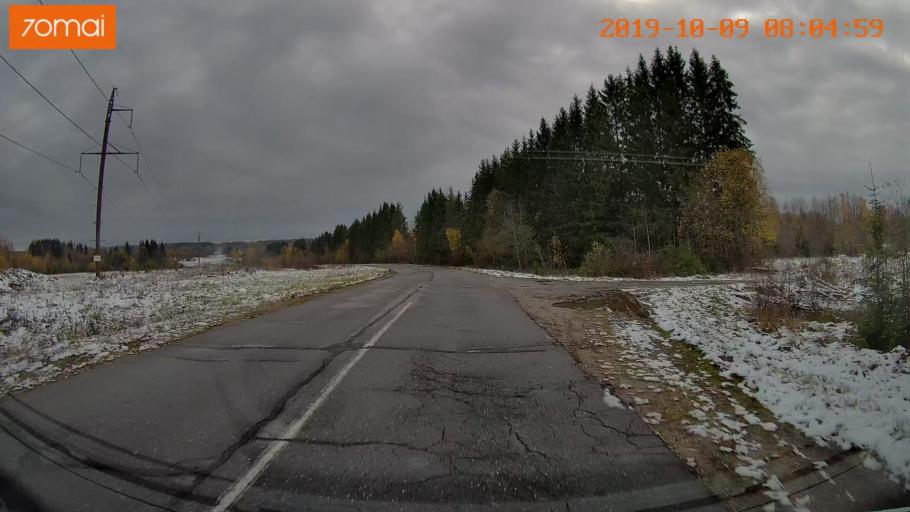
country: RU
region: Jaroslavl
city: Kukoboy
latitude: 58.6908
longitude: 40.0360
